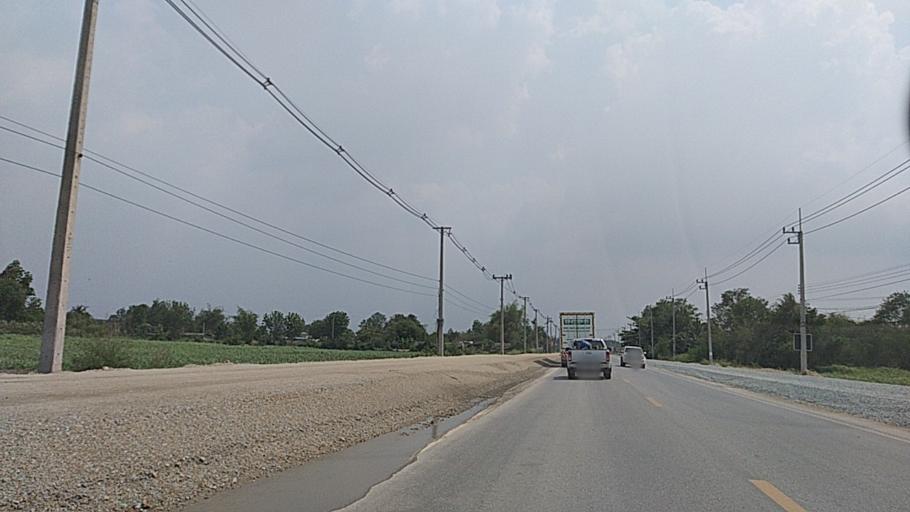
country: TH
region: Chon Buri
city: Phanat Nikhom
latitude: 13.3706
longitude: 101.1954
